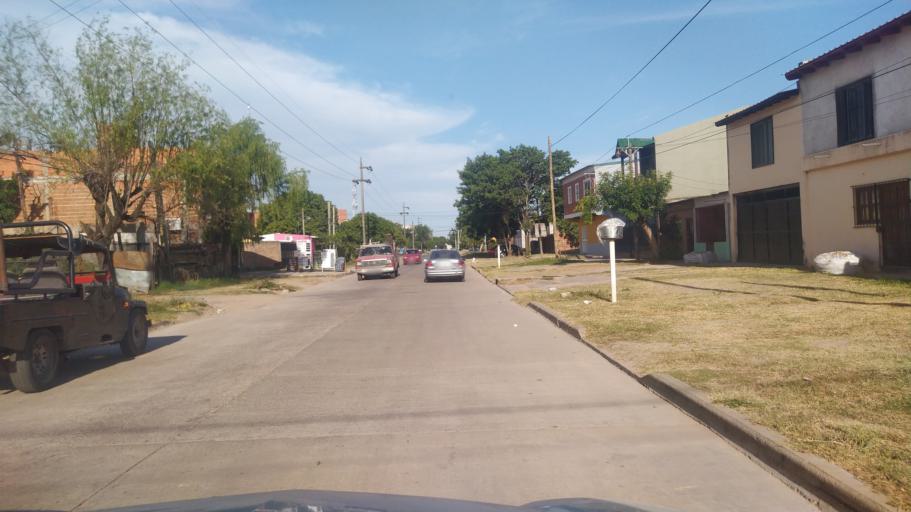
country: AR
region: Corrientes
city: Corrientes
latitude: -27.4825
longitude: -58.8020
